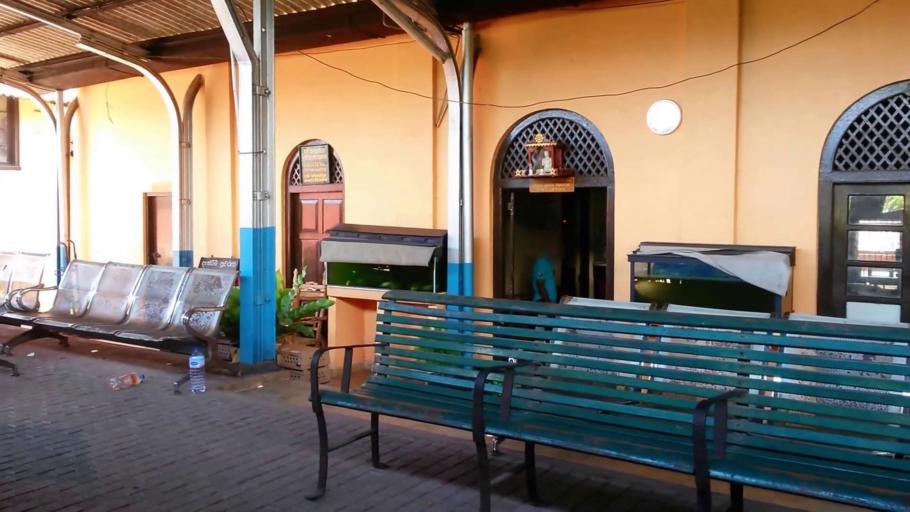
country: LK
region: Southern
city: Hikkaduwa
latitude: 6.1459
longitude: 80.1010
